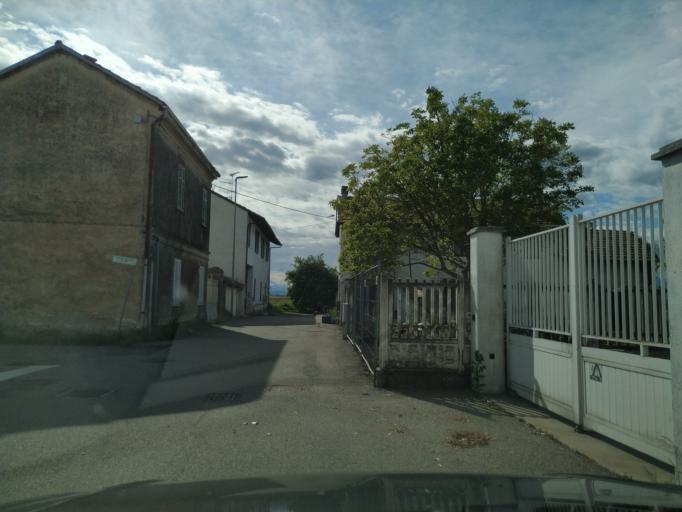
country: IT
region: Piedmont
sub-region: Provincia di Vercelli
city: Olcenengo
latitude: 45.3624
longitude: 8.3075
